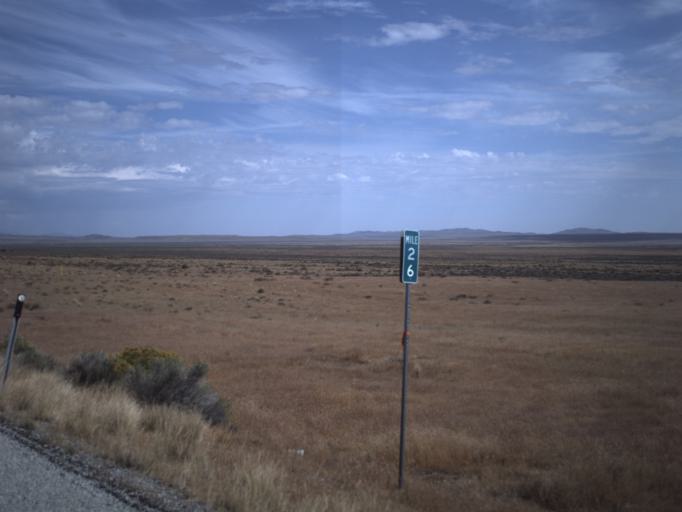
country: US
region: Utah
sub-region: Tooele County
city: Wendover
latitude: 41.5117
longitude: -113.6005
